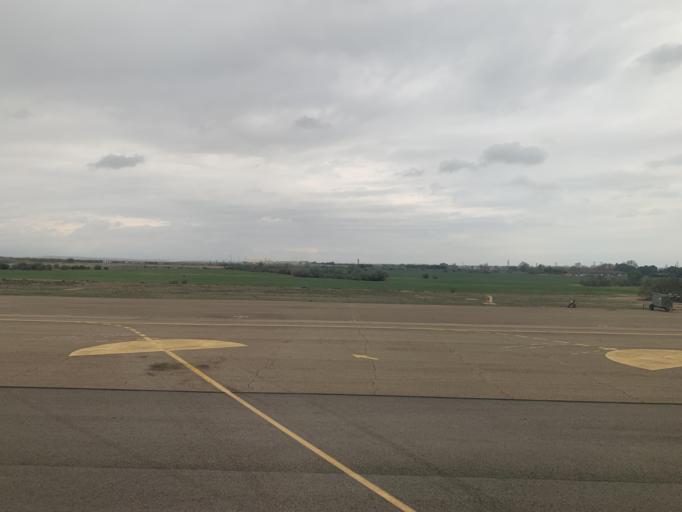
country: ES
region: Aragon
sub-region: Provincia de Zaragoza
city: Utebo
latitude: 41.6703
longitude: -1.0387
